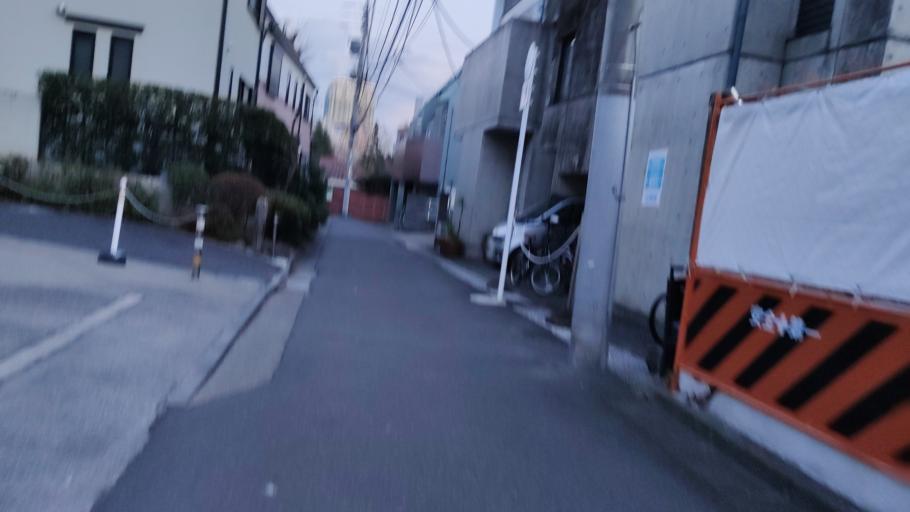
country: JP
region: Tokyo
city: Tokyo
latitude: 35.6414
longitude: 139.7241
